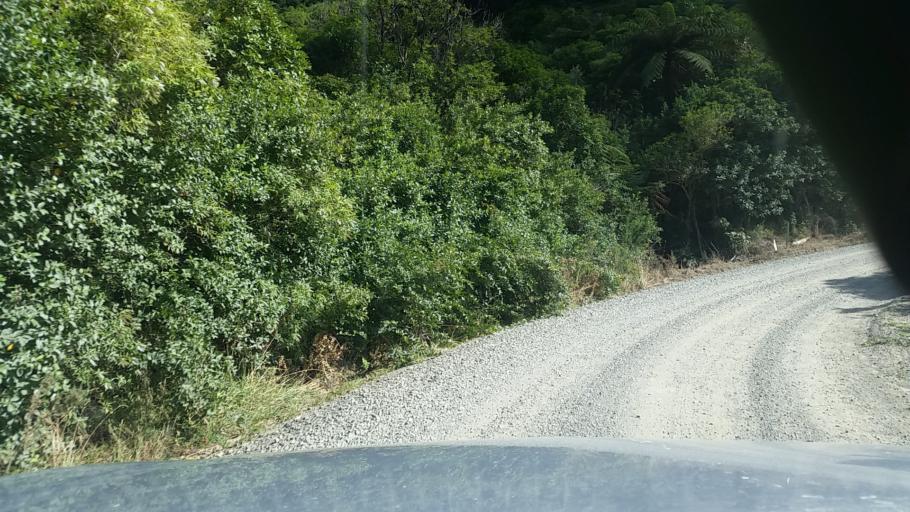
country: NZ
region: Marlborough
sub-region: Marlborough District
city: Picton
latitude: -41.2851
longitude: 174.1319
